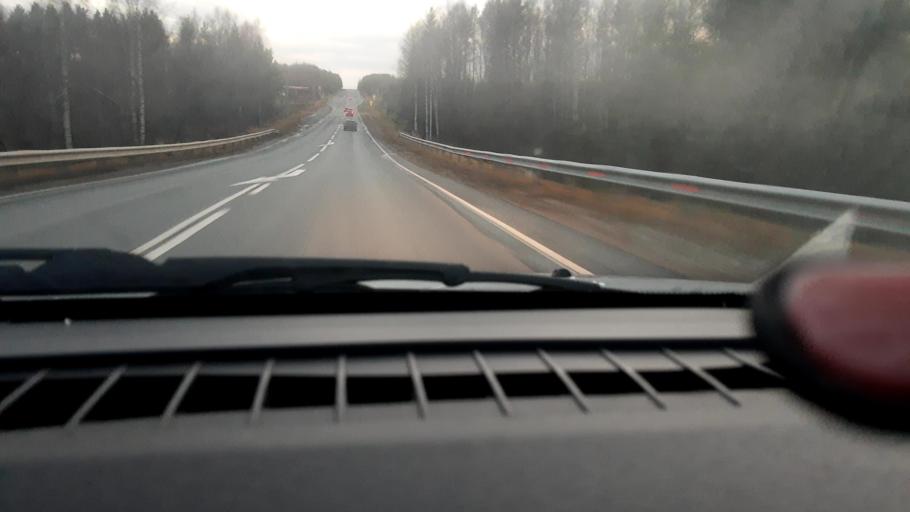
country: RU
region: Nizjnij Novgorod
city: Vladimirskoye
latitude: 56.9763
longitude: 45.1139
